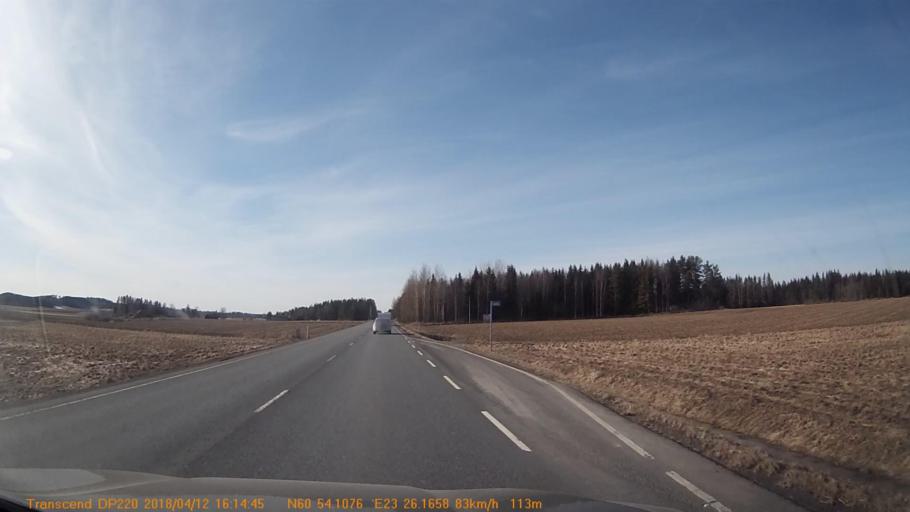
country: FI
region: Haeme
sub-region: Forssa
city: Humppila
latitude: 60.9018
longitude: 23.4360
